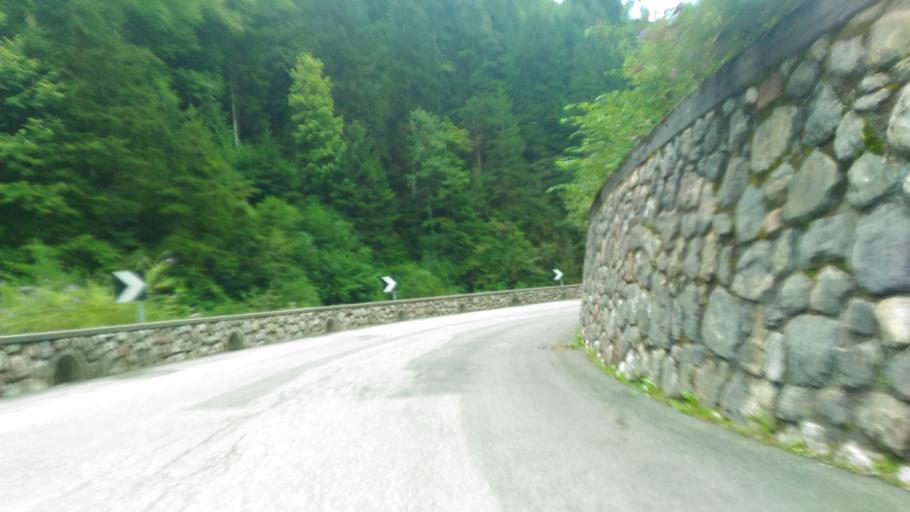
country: IT
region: Lombardy
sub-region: Provincia di Bergamo
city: Mezzoldo
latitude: 46.0005
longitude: 9.6733
